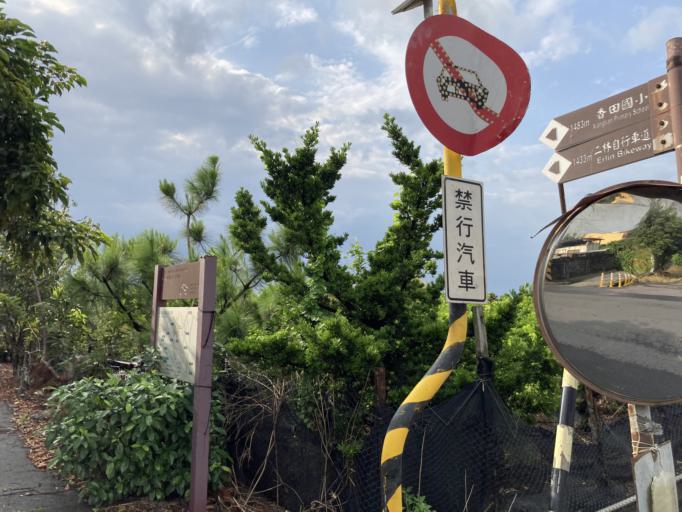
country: TW
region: Taiwan
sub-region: Yunlin
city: Douliu
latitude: 23.8790
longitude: 120.3627
